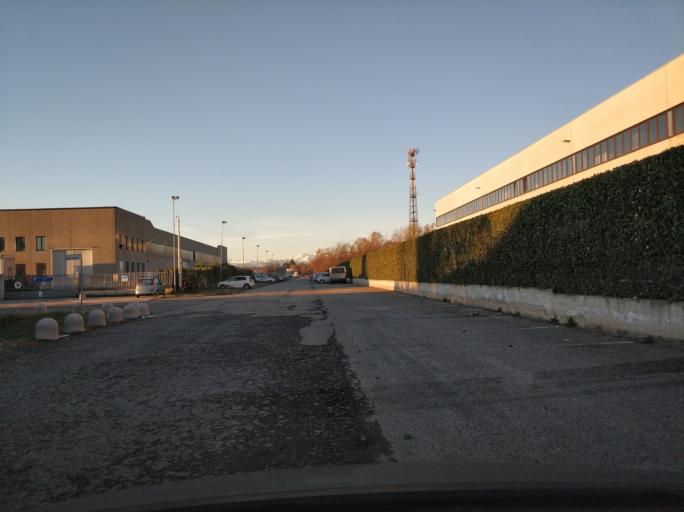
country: IT
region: Piedmont
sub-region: Provincia di Torino
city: Robassomero
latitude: 45.1796
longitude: 7.5978
